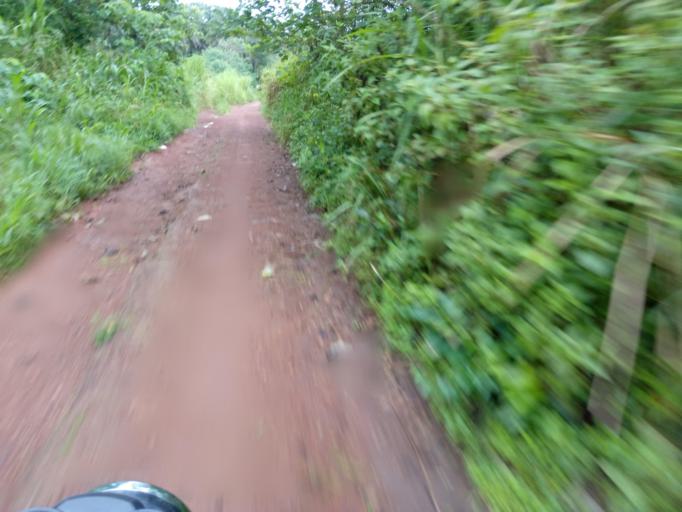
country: SL
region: Eastern Province
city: Buedu
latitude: 8.4690
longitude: -10.3456
